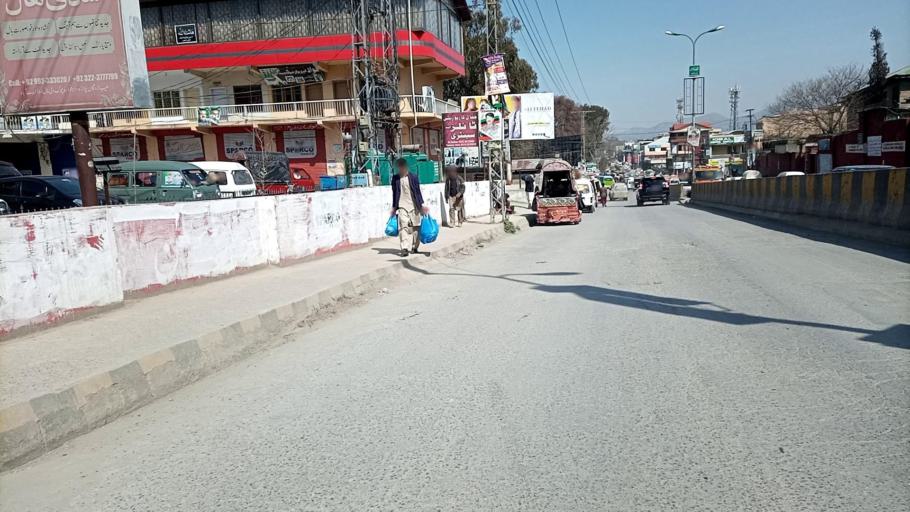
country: PK
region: Khyber Pakhtunkhwa
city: Abbottabad
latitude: 34.1426
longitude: 73.2141
